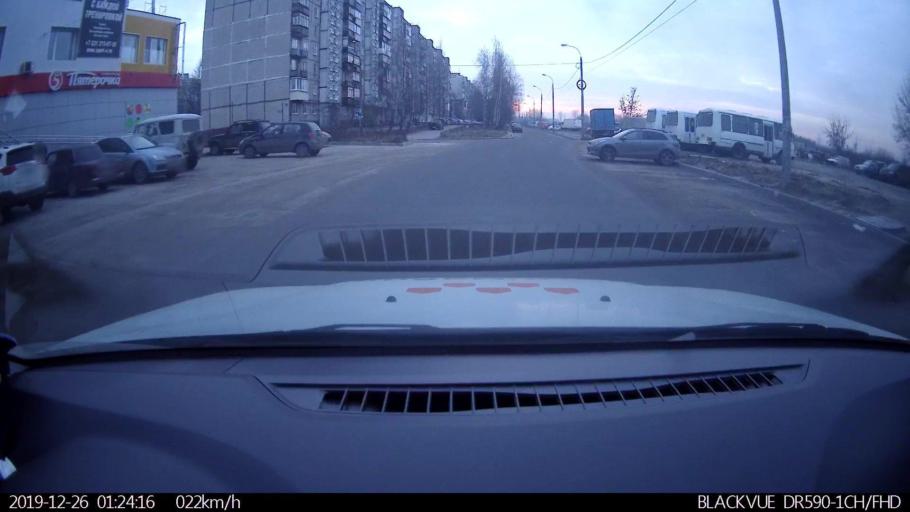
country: RU
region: Nizjnij Novgorod
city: Gorbatovka
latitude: 56.2726
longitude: 43.8775
